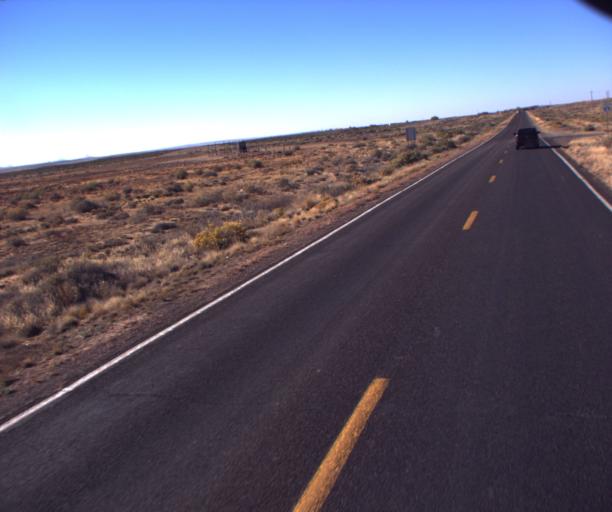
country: US
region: Arizona
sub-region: Navajo County
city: First Mesa
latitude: 35.8128
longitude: -110.4090
